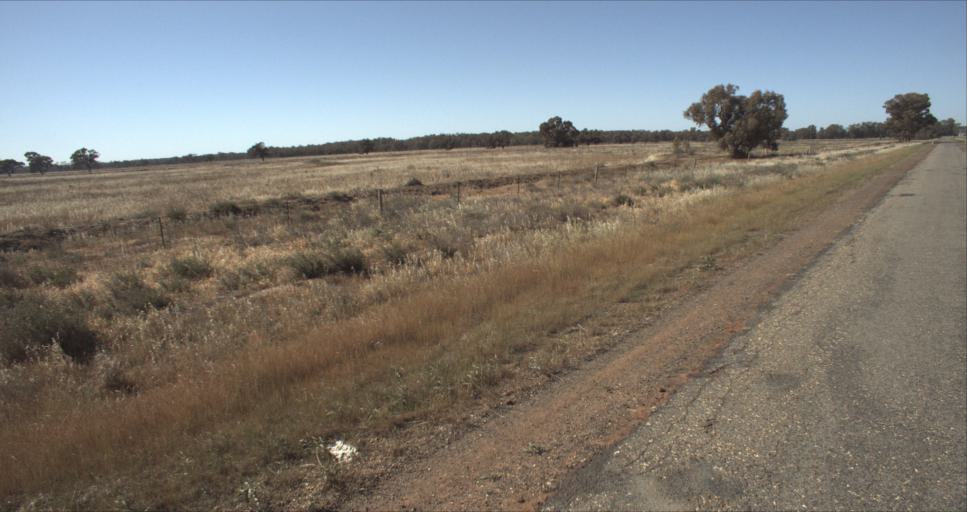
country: AU
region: New South Wales
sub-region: Leeton
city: Leeton
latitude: -34.5961
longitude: 146.2587
